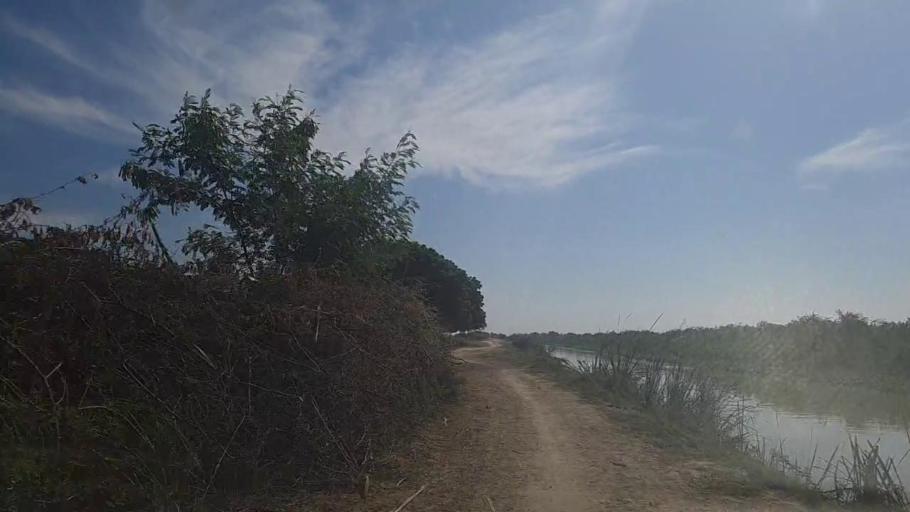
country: PK
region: Sindh
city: Mirpur Batoro
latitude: 24.6598
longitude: 68.1943
